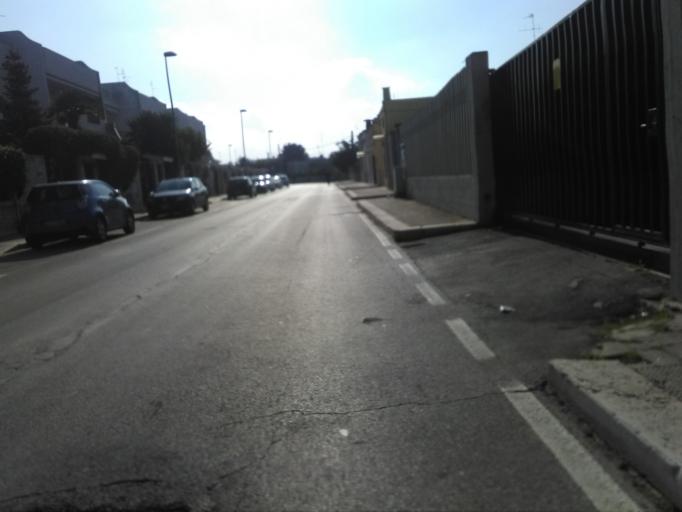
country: IT
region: Apulia
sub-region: Provincia di Bari
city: San Paolo
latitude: 41.1582
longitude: 16.7621
